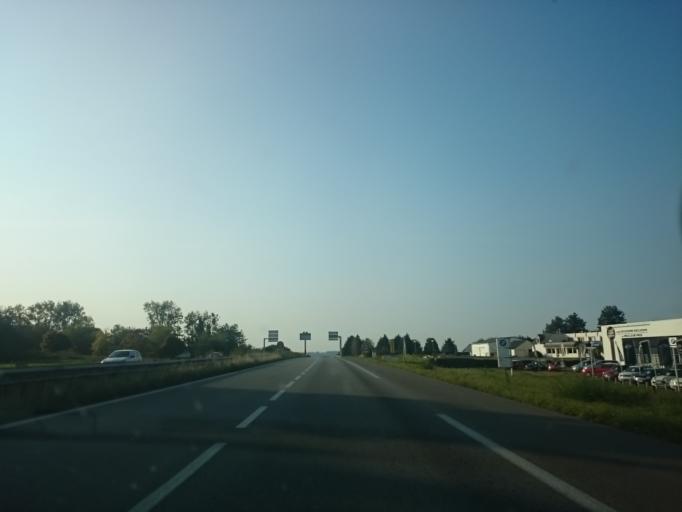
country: FR
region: Brittany
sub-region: Departement du Finistere
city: Morlaix
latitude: 48.5920
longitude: -3.8172
